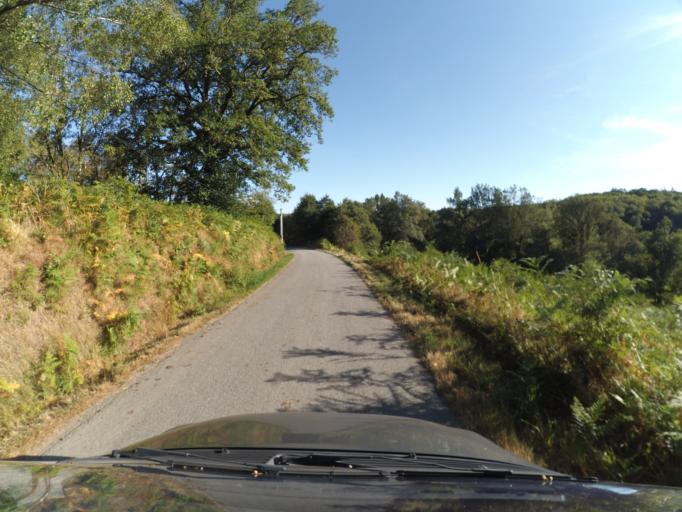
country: FR
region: Limousin
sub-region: Departement de la Creuse
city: Banize
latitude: 45.7689
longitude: 2.0170
